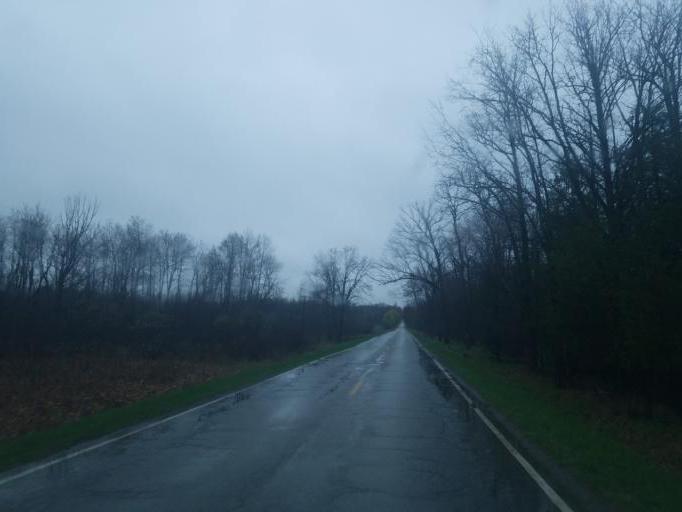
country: US
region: Michigan
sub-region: Montcalm County
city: Edmore
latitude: 43.5108
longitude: -85.0257
